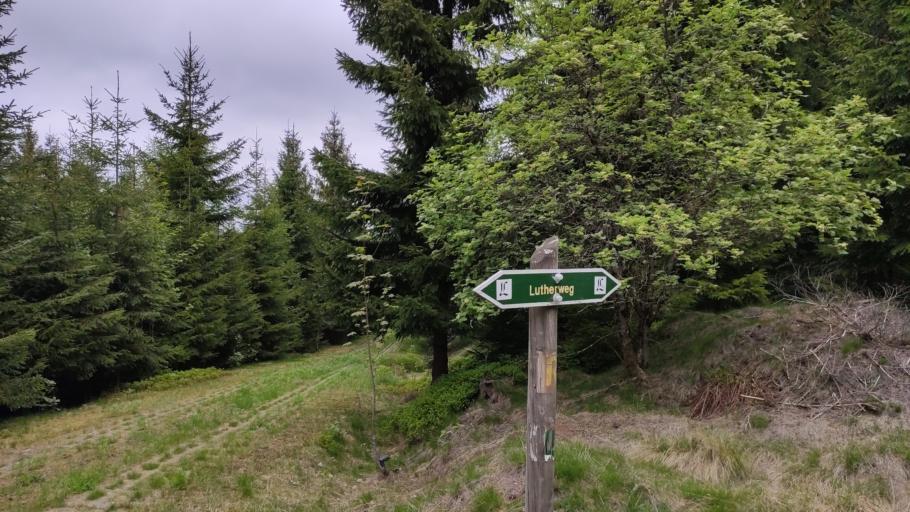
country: DE
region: Bavaria
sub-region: Upper Franconia
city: Reichenbach
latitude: 50.4488
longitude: 11.4202
